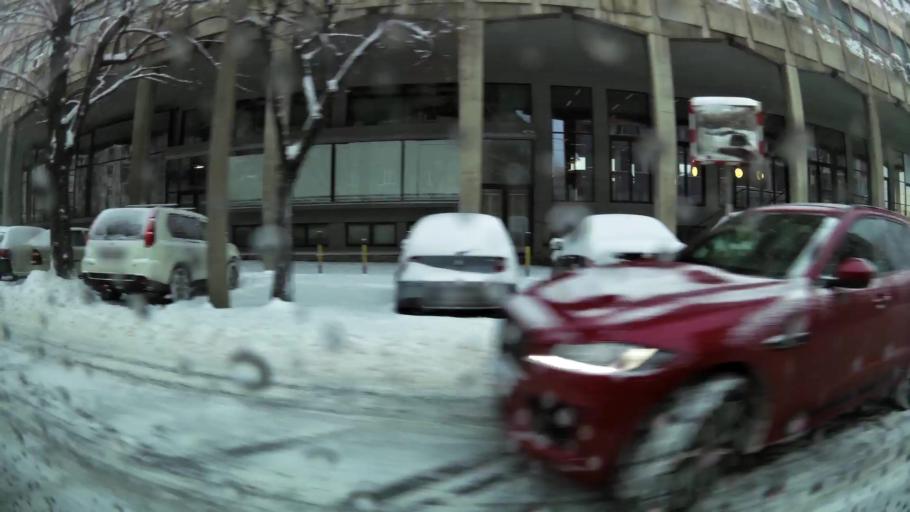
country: RS
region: Central Serbia
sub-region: Belgrade
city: Stari Grad
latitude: 44.8220
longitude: 20.4693
